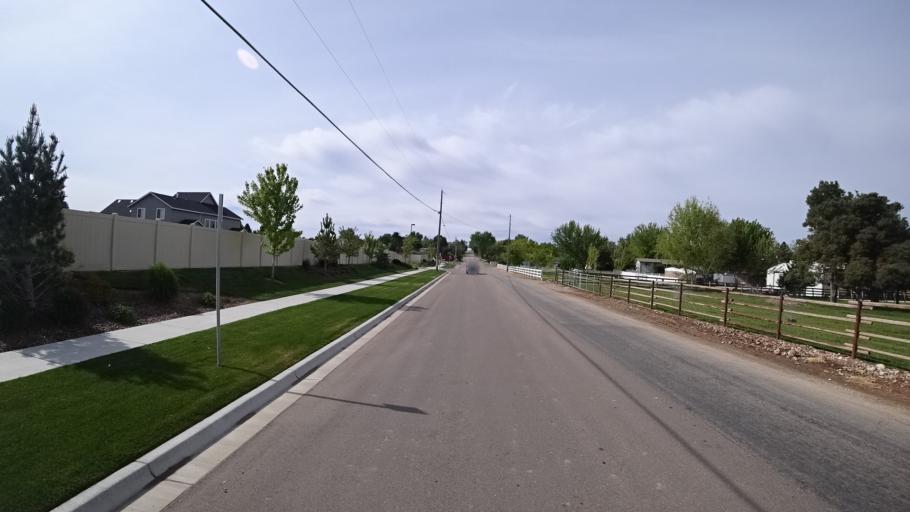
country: US
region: Idaho
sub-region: Ada County
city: Garden City
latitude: 43.5741
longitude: -116.3041
